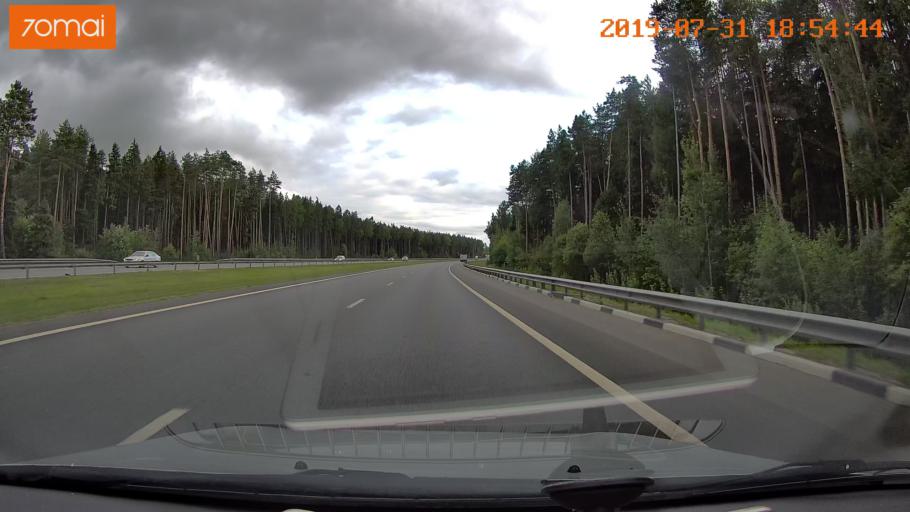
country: RU
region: Moskovskaya
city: Raduzhnyy
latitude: 55.1853
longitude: 38.6695
